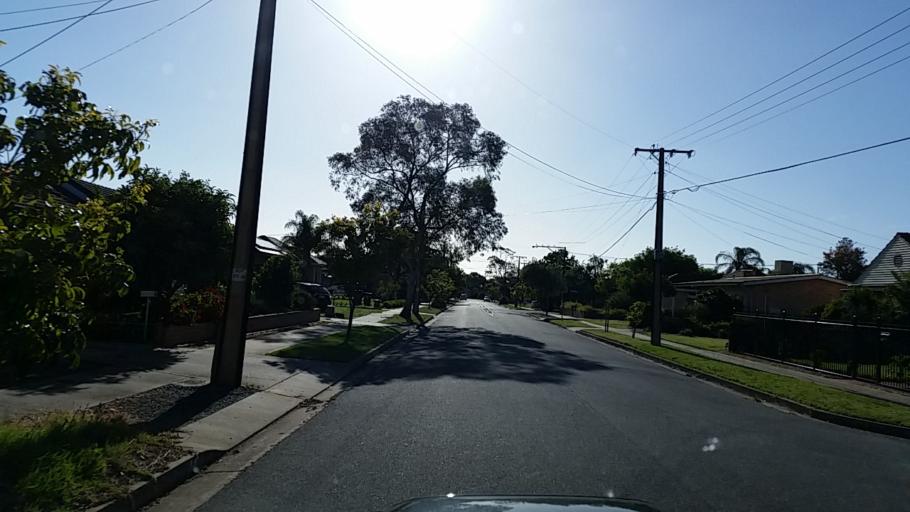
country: AU
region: South Australia
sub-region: Marion
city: South Plympton
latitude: -34.9784
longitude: 138.5622
